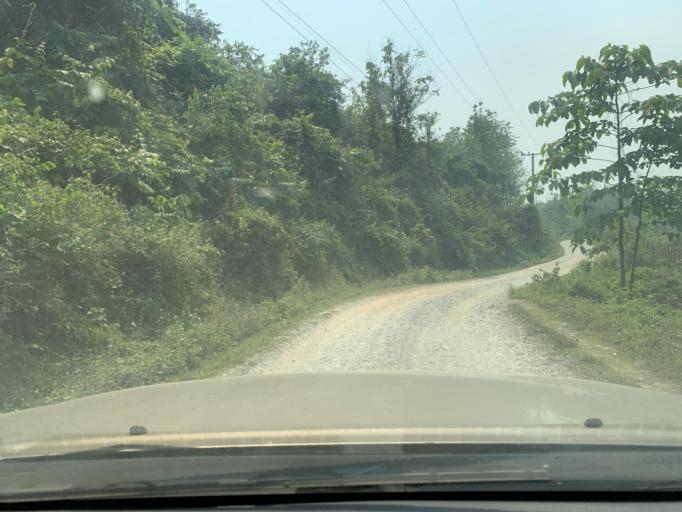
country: LA
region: Louangphabang
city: Louangphabang
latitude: 19.8820
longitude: 102.2599
